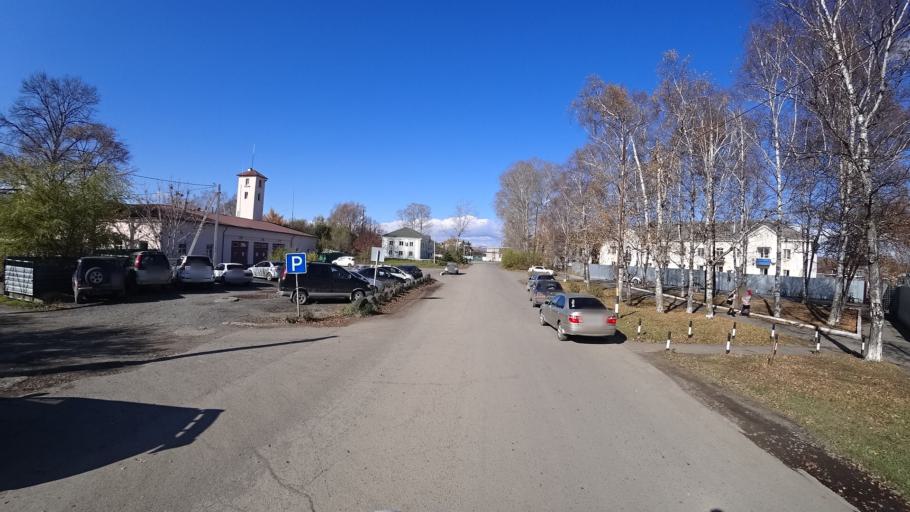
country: RU
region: Khabarovsk Krai
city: Amursk
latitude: 50.0992
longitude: 136.4913
